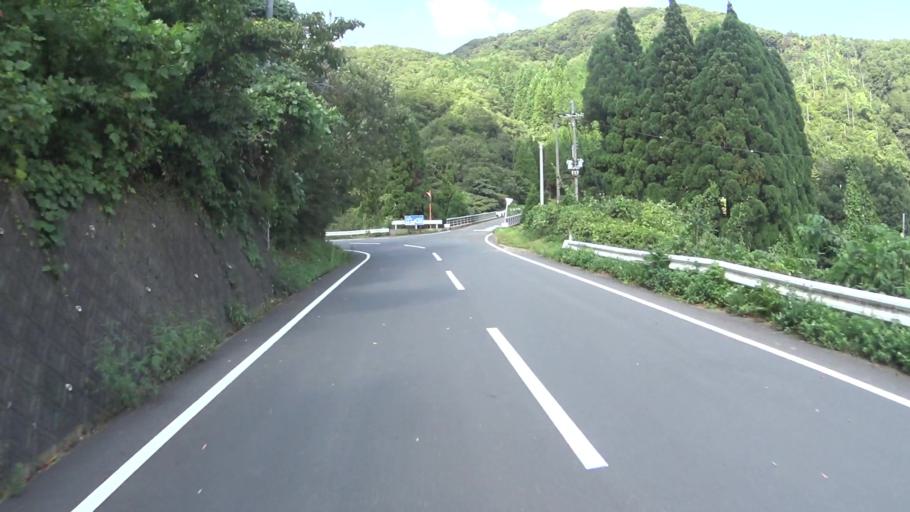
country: JP
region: Kyoto
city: Miyazu
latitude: 35.7084
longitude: 135.2455
